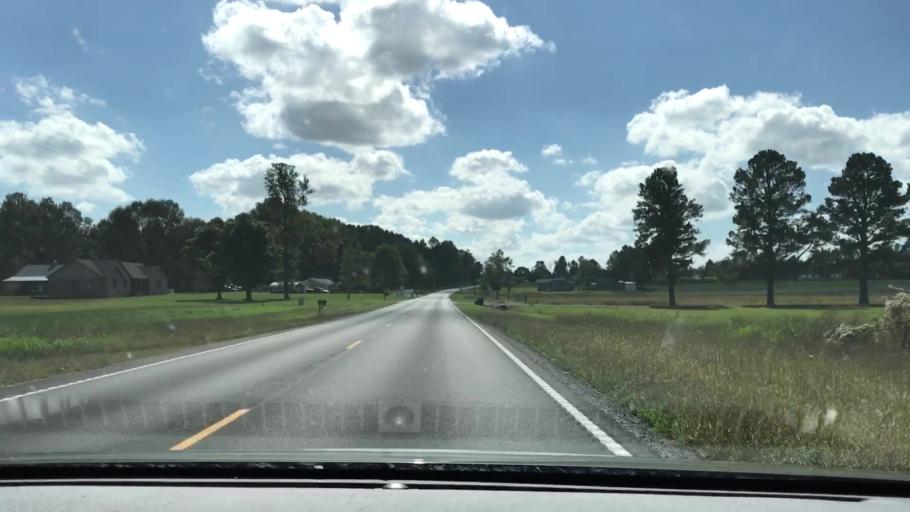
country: US
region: Kentucky
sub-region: Graves County
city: Mayfield
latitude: 36.8596
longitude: -88.5720
